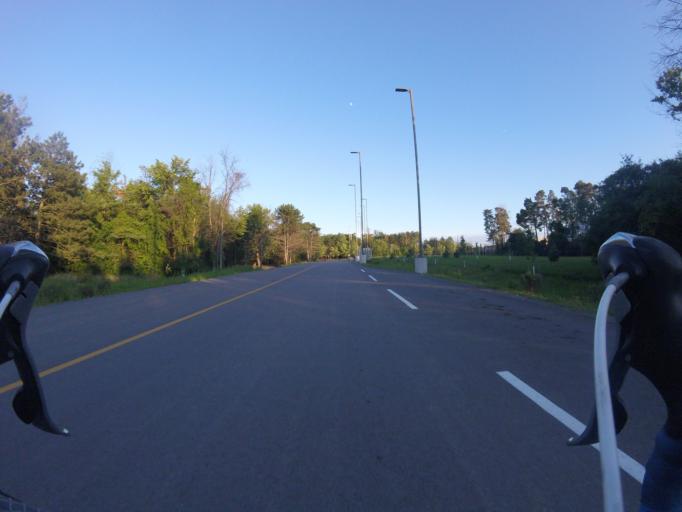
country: CA
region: Ontario
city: Bells Corners
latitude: 45.3518
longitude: -75.8479
